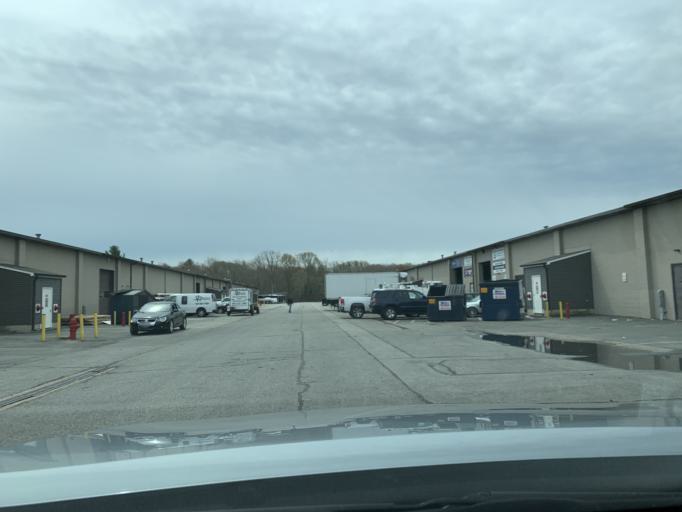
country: US
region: Rhode Island
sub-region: Washington County
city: North Kingstown
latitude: 41.6039
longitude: -71.4774
